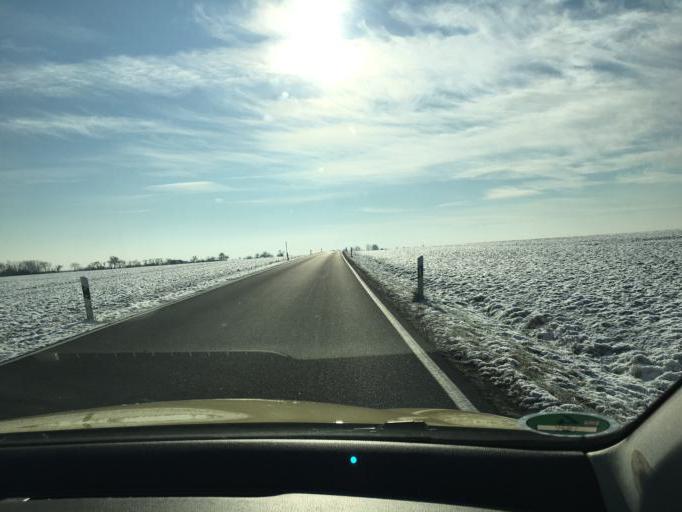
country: DE
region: Saxony
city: Belgershain
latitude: 51.2487
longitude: 12.5443
